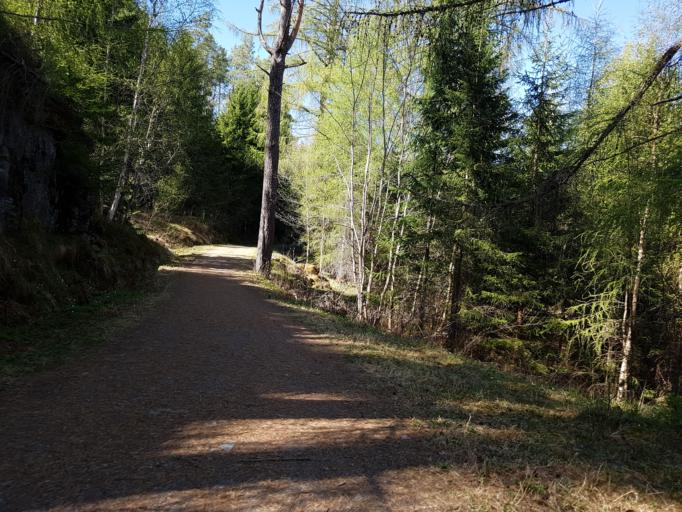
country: NO
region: Sor-Trondelag
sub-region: Trondheim
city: Trondheim
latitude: 63.4368
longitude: 10.3435
